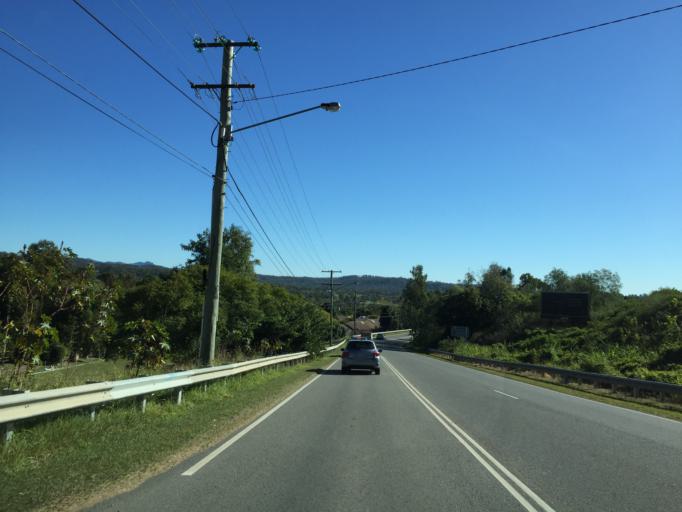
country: AU
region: Queensland
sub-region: Moreton Bay
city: Ferny Hills
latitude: -27.4229
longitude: 152.9484
